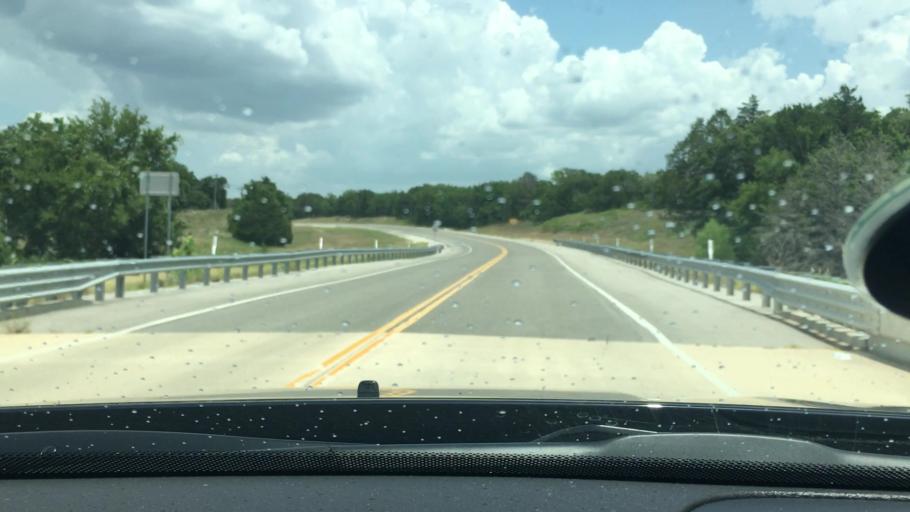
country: US
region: Oklahoma
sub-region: Love County
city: Marietta
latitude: 33.9732
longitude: -96.9930
